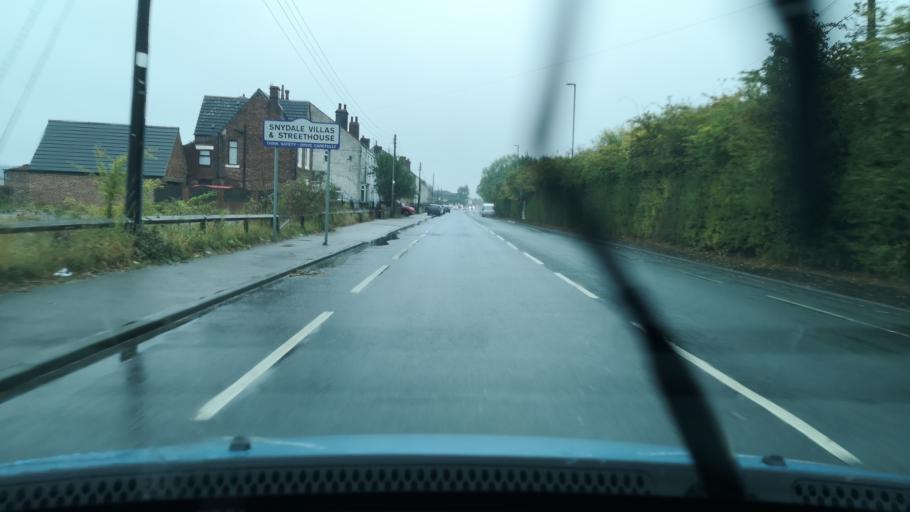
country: GB
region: England
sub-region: City and Borough of Wakefield
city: Sharlston
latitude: 53.6756
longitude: -1.3883
